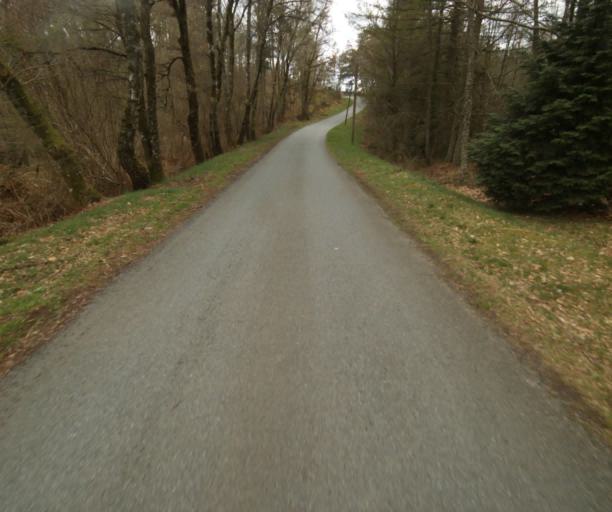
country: FR
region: Limousin
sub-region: Departement de la Correze
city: Correze
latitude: 45.3148
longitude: 1.9323
